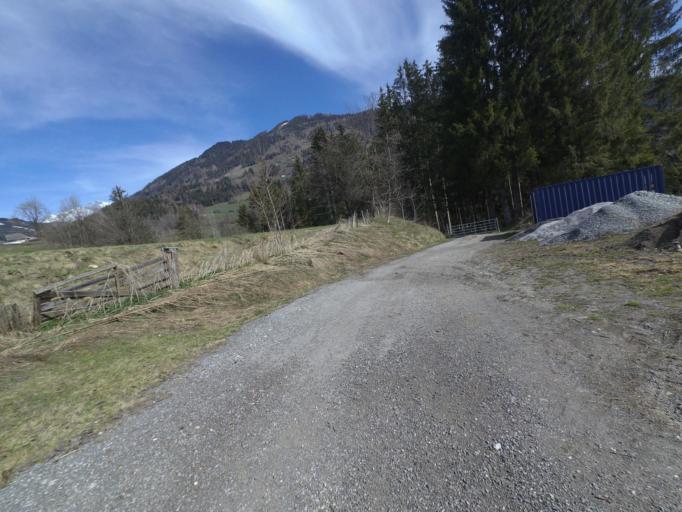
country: AT
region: Salzburg
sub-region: Politischer Bezirk Sankt Johann im Pongau
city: Sankt Veit im Pongau
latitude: 47.3255
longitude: 13.1354
